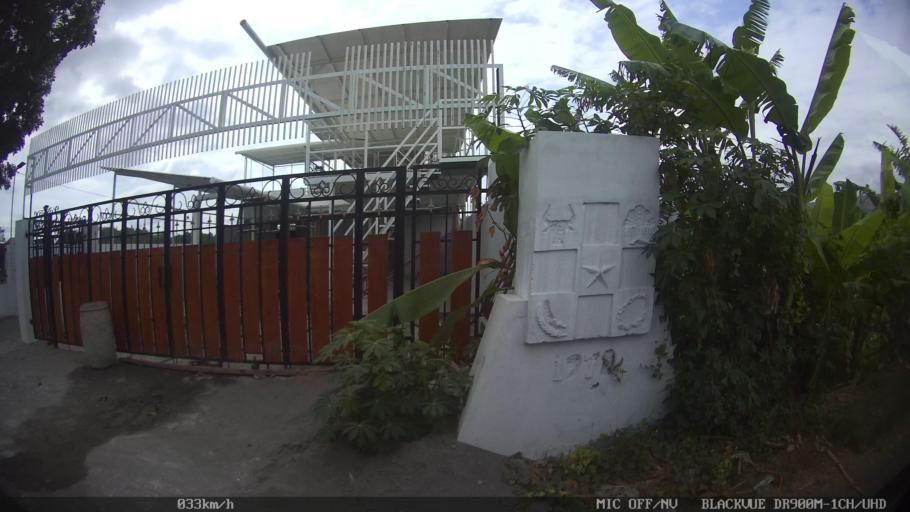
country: ID
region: Daerah Istimewa Yogyakarta
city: Depok
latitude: -7.8222
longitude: 110.4643
